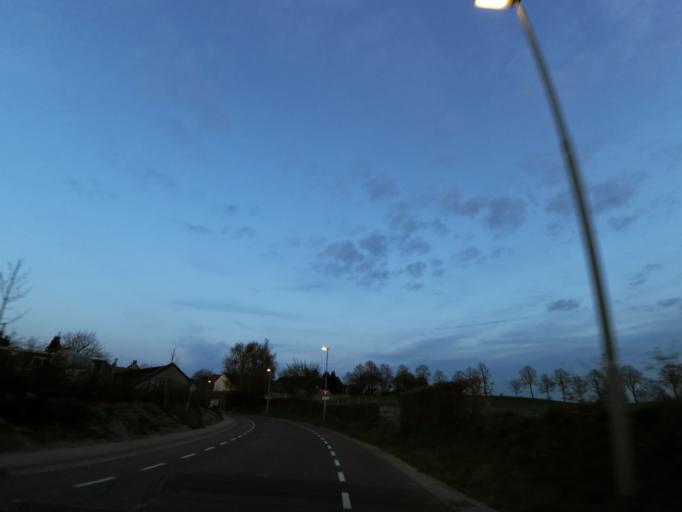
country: NL
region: Limburg
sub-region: Gemeente Voerendaal
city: Ubachsberg
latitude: 50.8462
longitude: 5.9666
